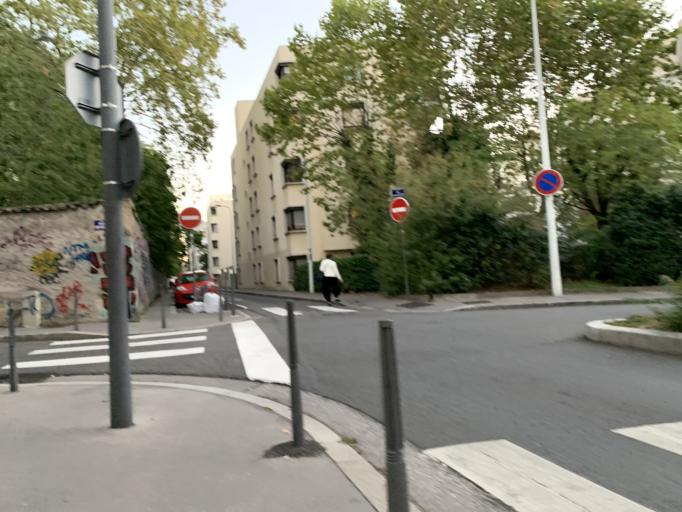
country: FR
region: Rhone-Alpes
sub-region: Departement du Rhone
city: Lyon
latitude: 45.7490
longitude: 4.8681
